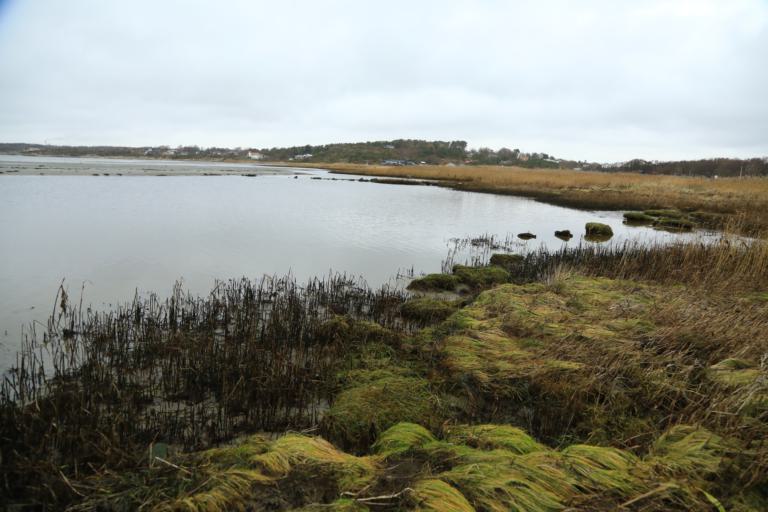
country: SE
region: Halland
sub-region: Varbergs Kommun
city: Varberg
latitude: 57.1805
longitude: 12.2130
